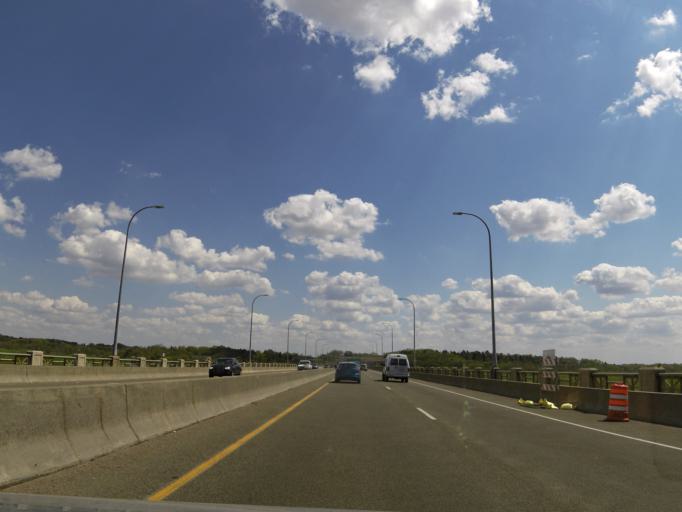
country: US
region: Minnesota
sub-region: Dakota County
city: Mendota Heights
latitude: 44.8890
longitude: -93.1805
